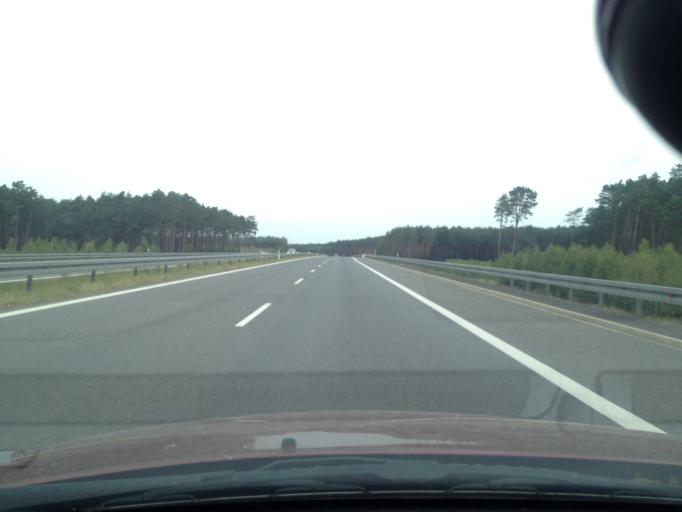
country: PL
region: Lubusz
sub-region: Powiat gorzowski
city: Deszczno
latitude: 52.6307
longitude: 15.3753
